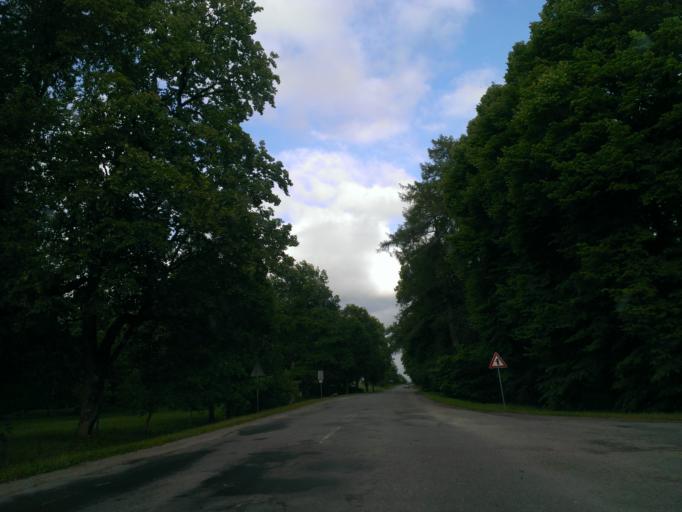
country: LV
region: Aizpute
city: Aizpute
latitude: 56.7296
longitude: 21.7338
